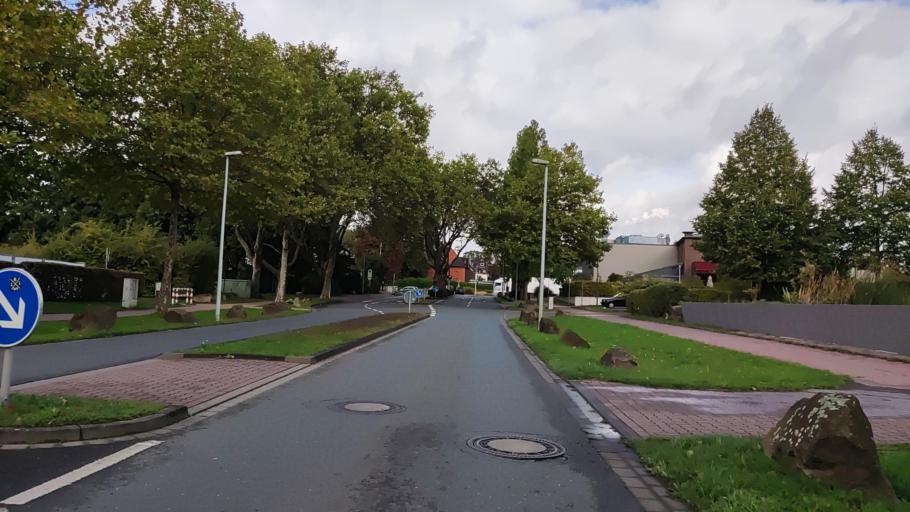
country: DE
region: North Rhine-Westphalia
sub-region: Regierungsbezirk Arnsberg
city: Herne
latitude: 51.5277
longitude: 7.2001
